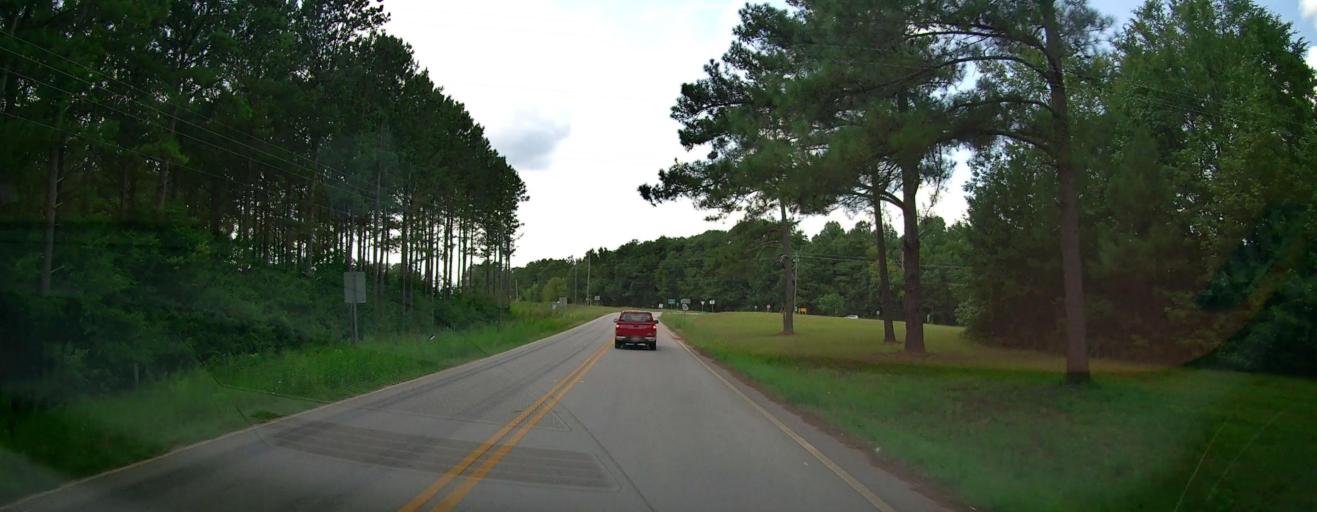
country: US
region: Georgia
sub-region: Troup County
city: Hogansville
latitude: 33.1583
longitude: -84.8610
